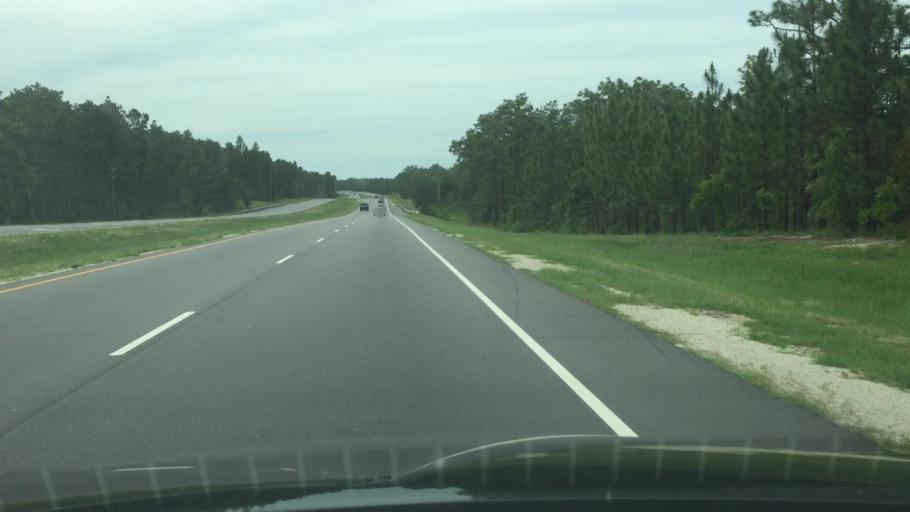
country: US
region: North Carolina
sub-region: Cumberland County
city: Spring Lake
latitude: 35.2206
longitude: -79.0043
